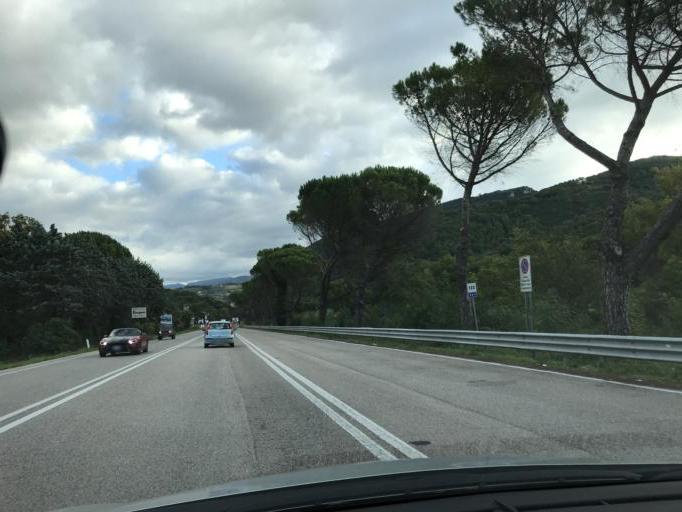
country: IT
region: Umbria
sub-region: Provincia di Perugia
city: Spoleto
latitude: 42.7178
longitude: 12.7265
